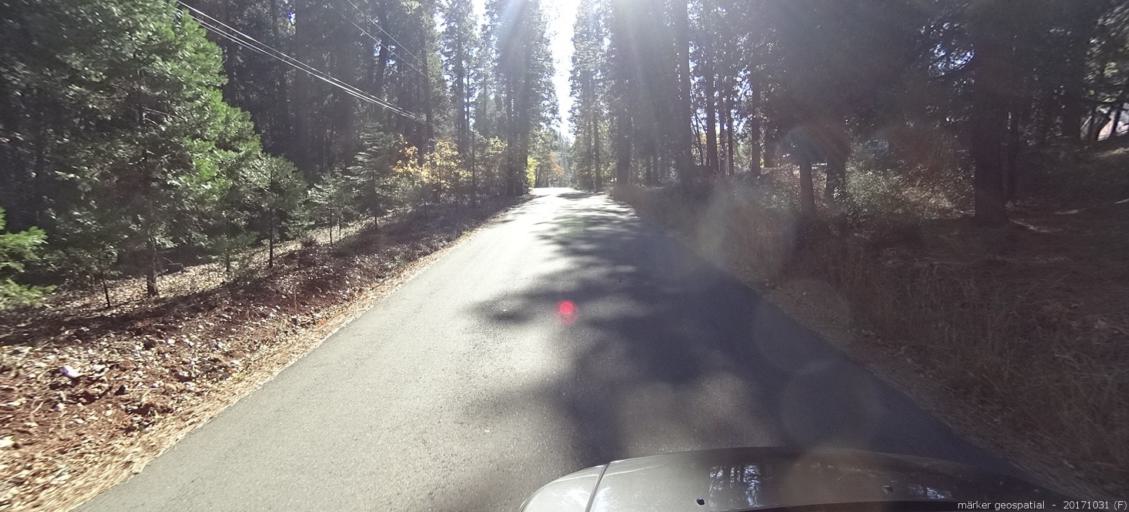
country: US
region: California
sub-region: Shasta County
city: Shingletown
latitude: 40.5143
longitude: -121.9360
